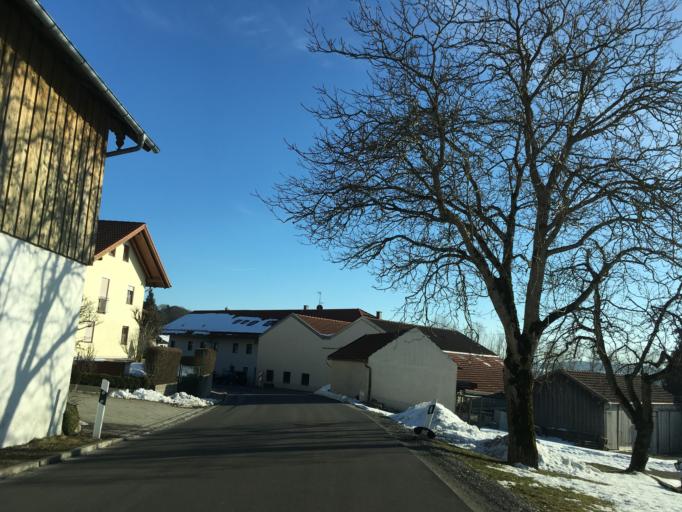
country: DE
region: Bavaria
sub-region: Upper Bavaria
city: Steinhoring
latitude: 48.1023
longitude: 12.0356
